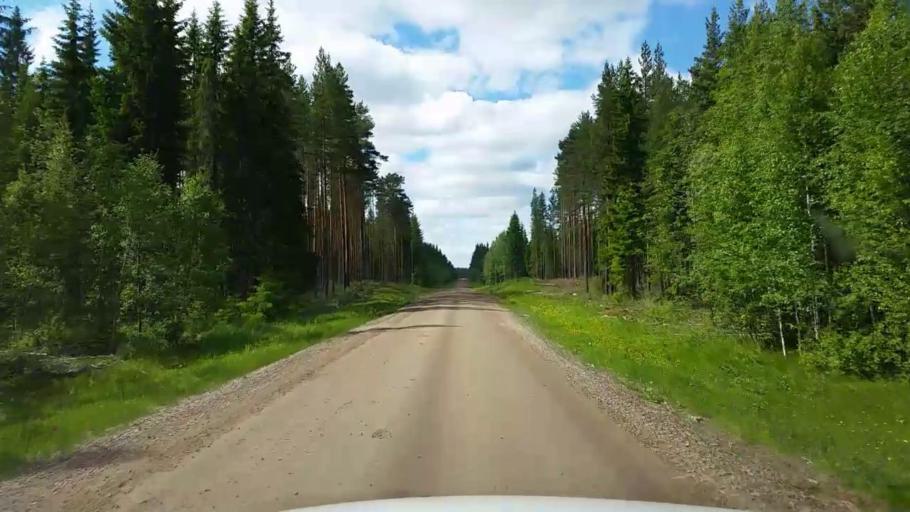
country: SE
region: Gaevleborg
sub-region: Ovanakers Kommun
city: Alfta
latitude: 61.4721
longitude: 16.0166
